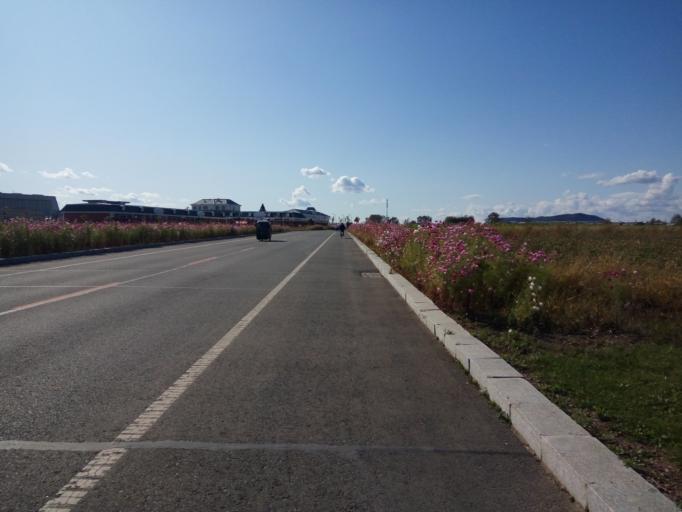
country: CN
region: Heilongjiang Sheng
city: Erjing
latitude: 48.6339
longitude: 126.1254
